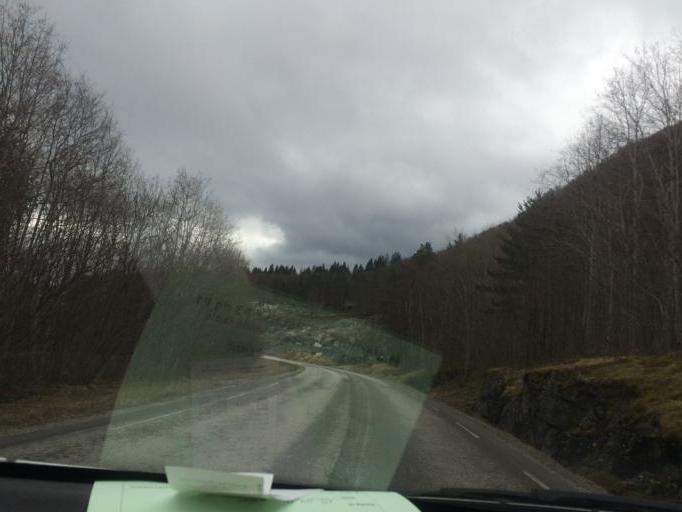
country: NO
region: More og Romsdal
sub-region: Gjemnes
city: Batnfjordsora
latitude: 62.9641
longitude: 7.7467
